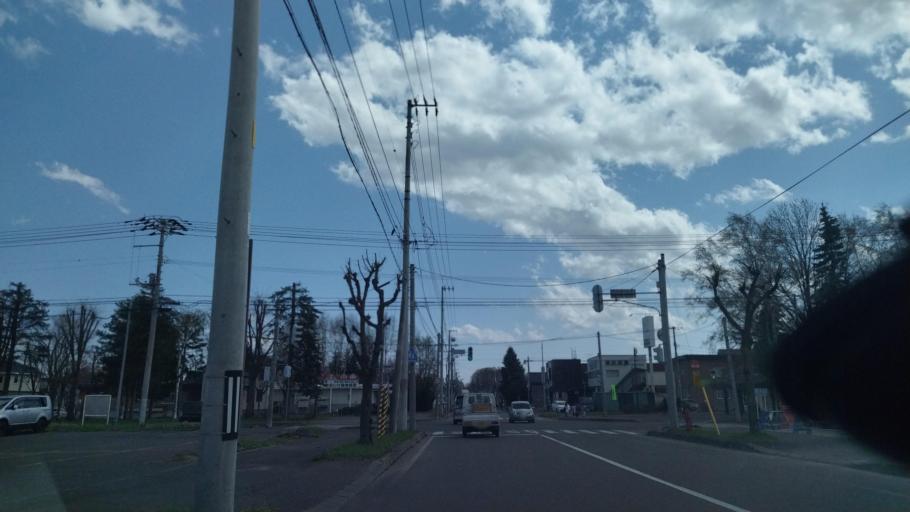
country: JP
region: Hokkaido
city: Obihiro
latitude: 42.9087
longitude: 143.1525
